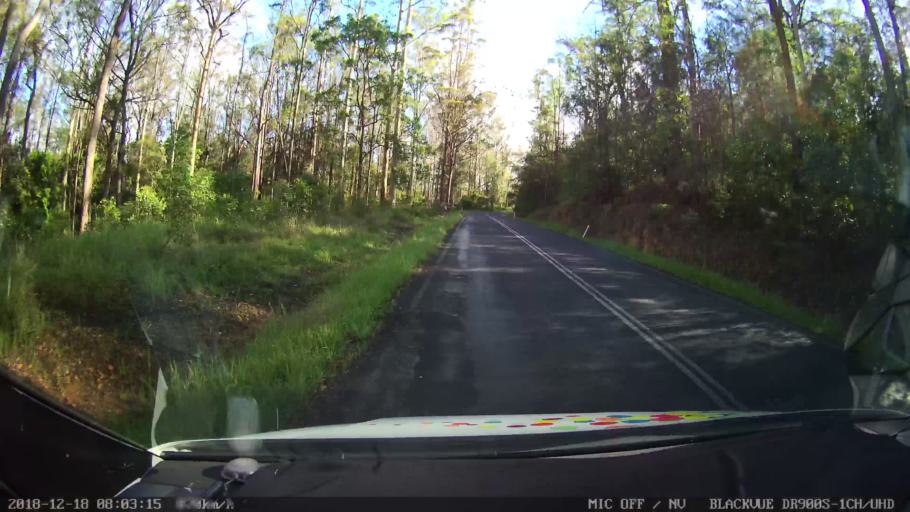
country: AU
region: New South Wales
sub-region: Kyogle
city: Kyogle
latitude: -28.3868
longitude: 152.6392
